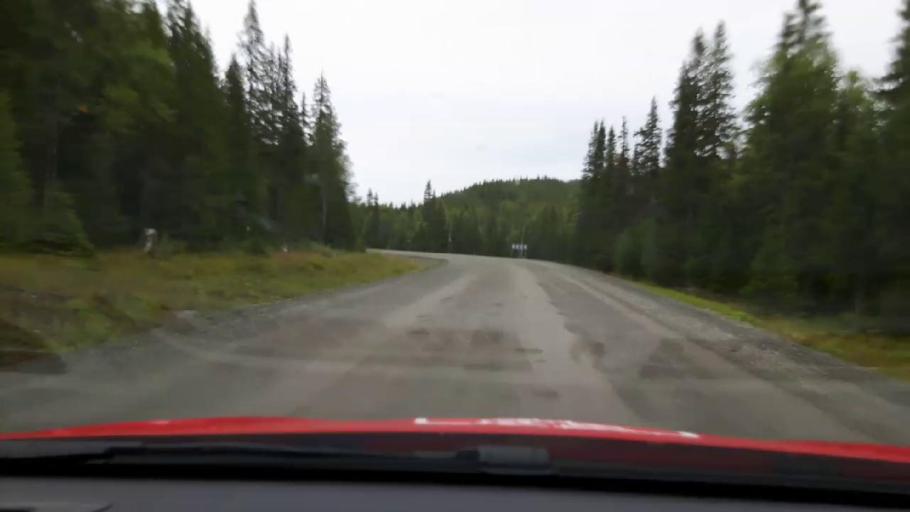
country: SE
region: Jaemtland
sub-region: Are Kommun
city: Are
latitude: 63.4239
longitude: 12.7417
